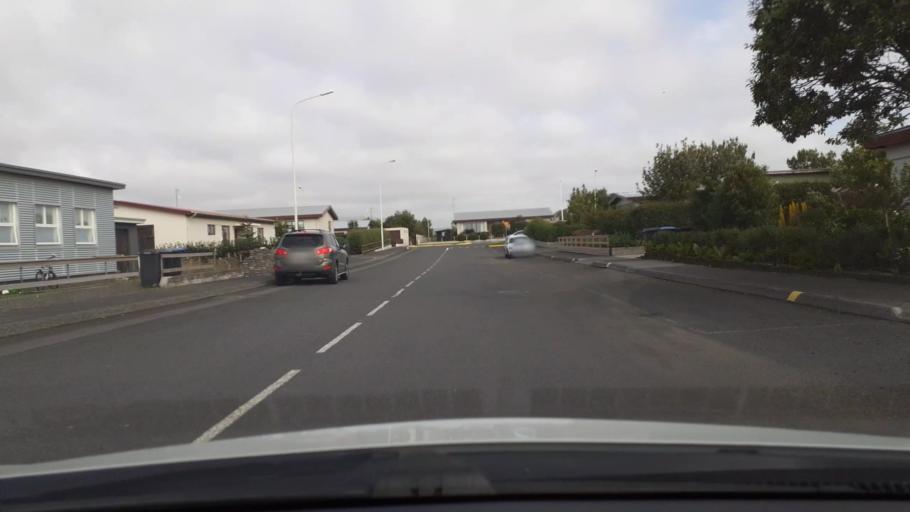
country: IS
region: South
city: THorlakshoefn
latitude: 63.8546
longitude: -21.3887
